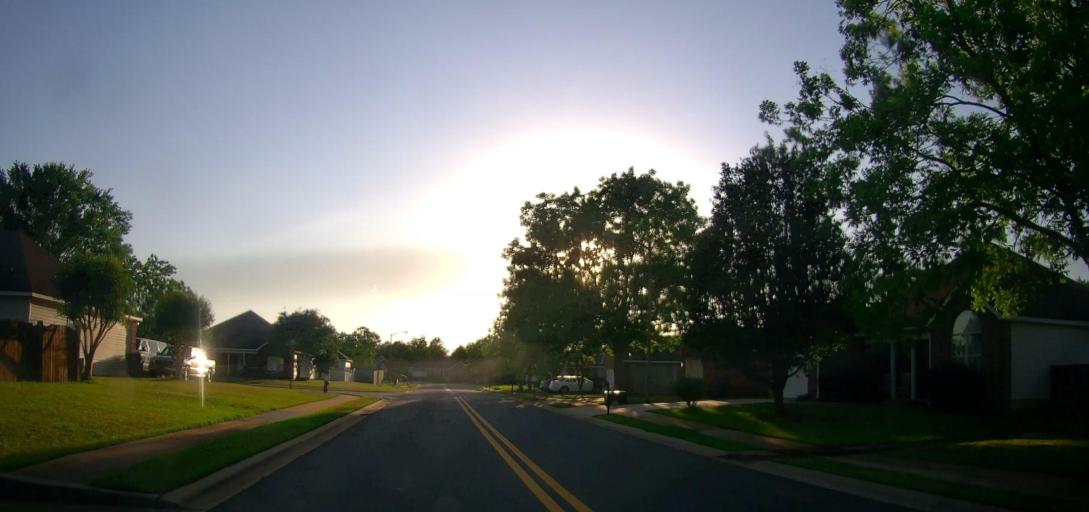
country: US
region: Georgia
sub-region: Houston County
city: Centerville
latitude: 32.6261
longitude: -83.7115
